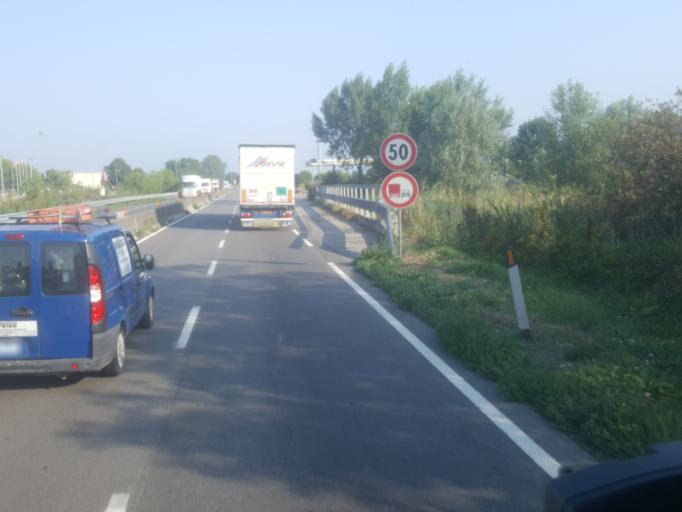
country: IT
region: Emilia-Romagna
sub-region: Provincia di Ravenna
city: Ravenna
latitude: 44.4138
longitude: 12.1705
